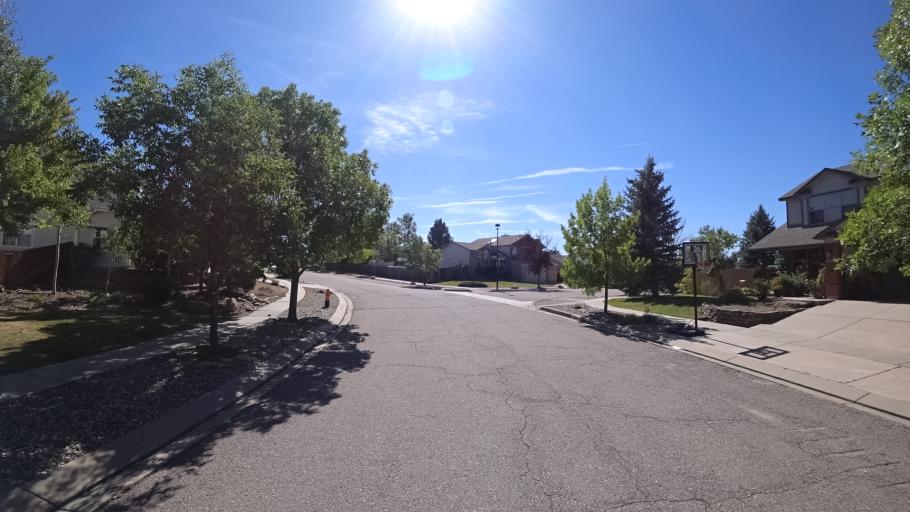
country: US
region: Colorado
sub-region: El Paso County
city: Black Forest
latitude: 38.9492
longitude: -104.7265
